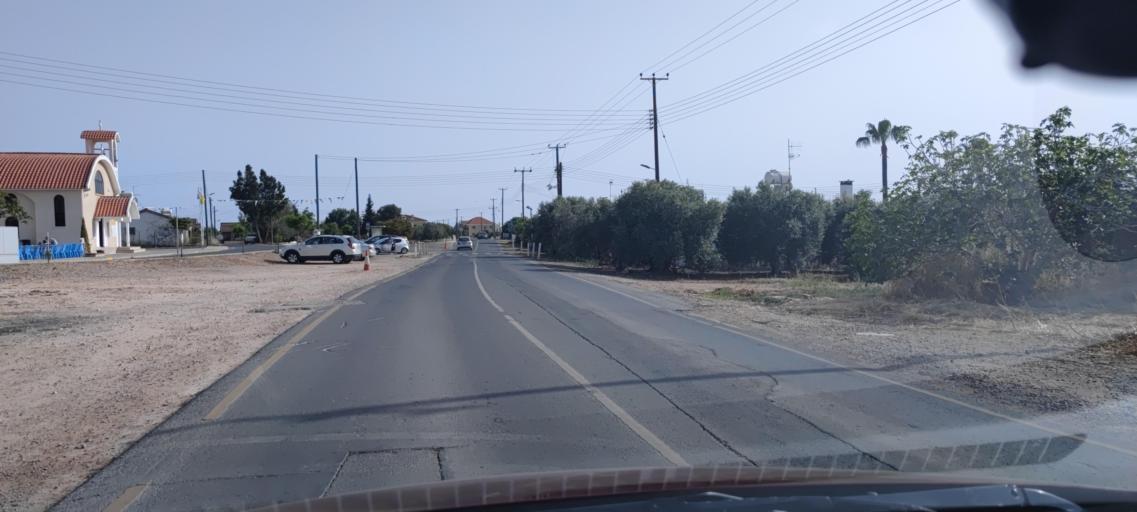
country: CY
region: Ammochostos
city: Deryneia
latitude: 35.0507
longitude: 33.9574
